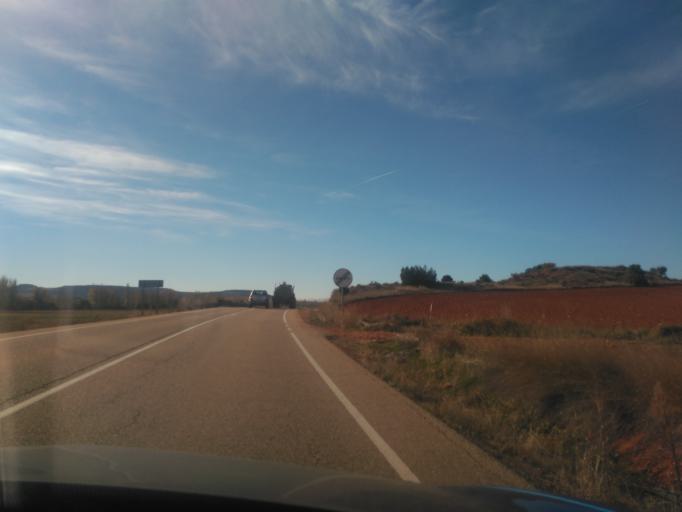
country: ES
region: Castille and Leon
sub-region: Provincia de Burgos
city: Huerta del Rey
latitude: 41.8045
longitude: -3.3373
